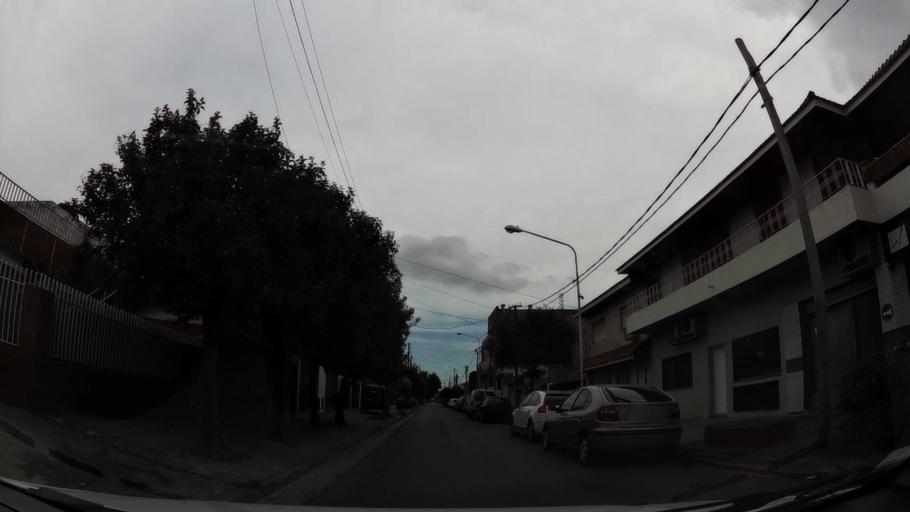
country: AR
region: Buenos Aires
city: San Justo
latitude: -34.6625
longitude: -58.5266
